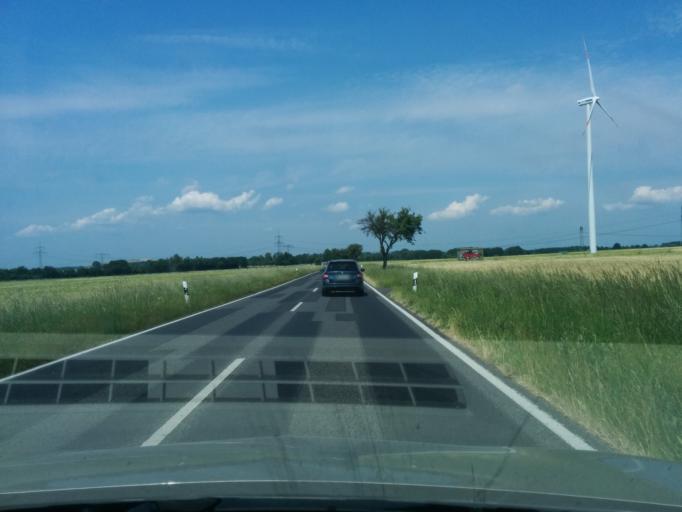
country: DE
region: Brandenburg
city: Ahrensfelde
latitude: 52.6164
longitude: 13.5884
